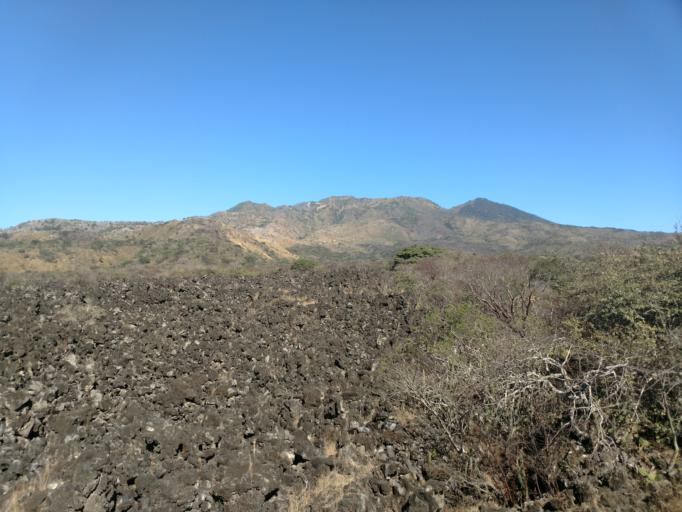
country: MX
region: Nayarit
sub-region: Ahuacatlan
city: Ahuacatlan
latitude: 21.0910
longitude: -104.5697
